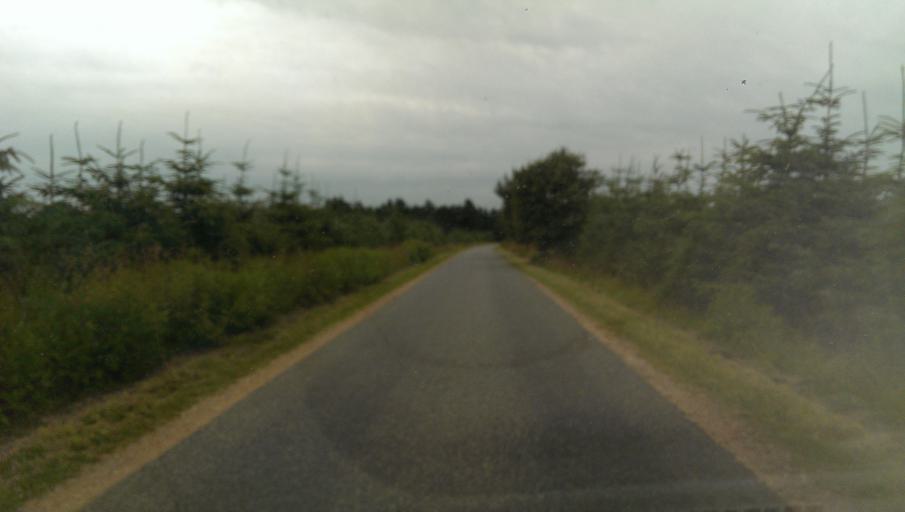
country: DK
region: South Denmark
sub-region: Esbjerg Kommune
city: Bramming
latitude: 55.4736
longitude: 8.7321
